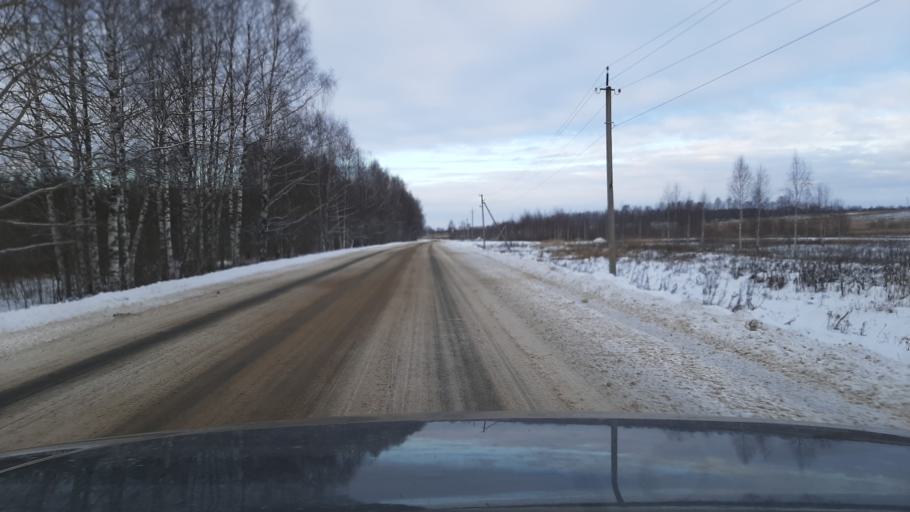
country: RU
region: Kostroma
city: Nerekhta
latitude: 57.4721
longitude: 40.6627
